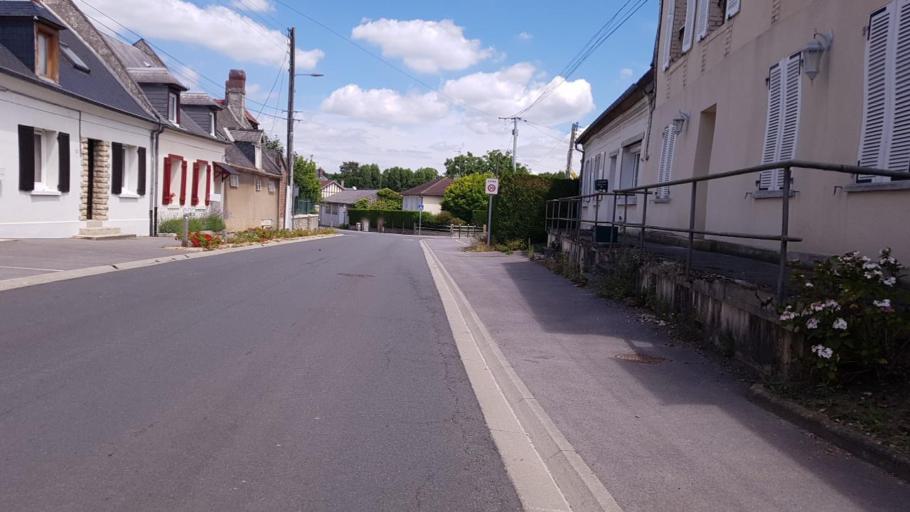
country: FR
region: Picardie
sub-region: Departement de l'Oise
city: Montmacq
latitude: 49.4797
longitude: 2.9524
